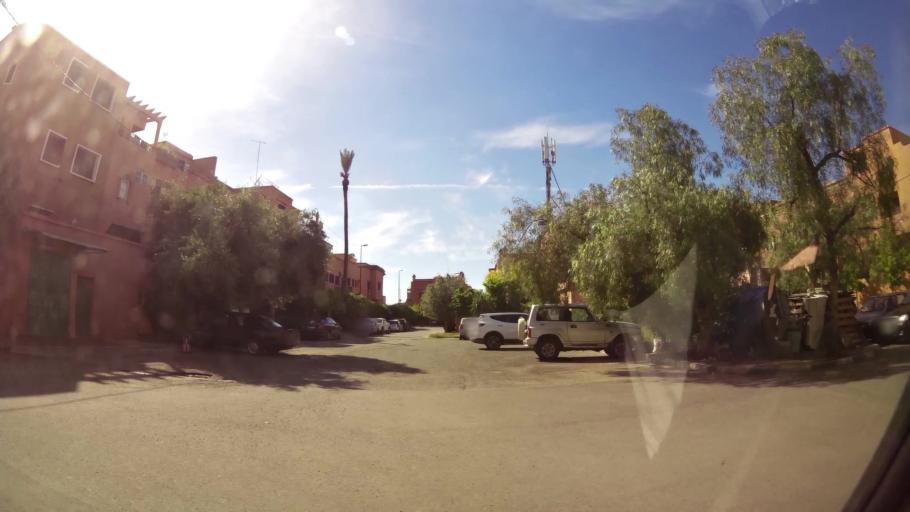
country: MA
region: Marrakech-Tensift-Al Haouz
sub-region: Marrakech
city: Marrakesh
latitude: 31.6530
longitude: -8.0127
